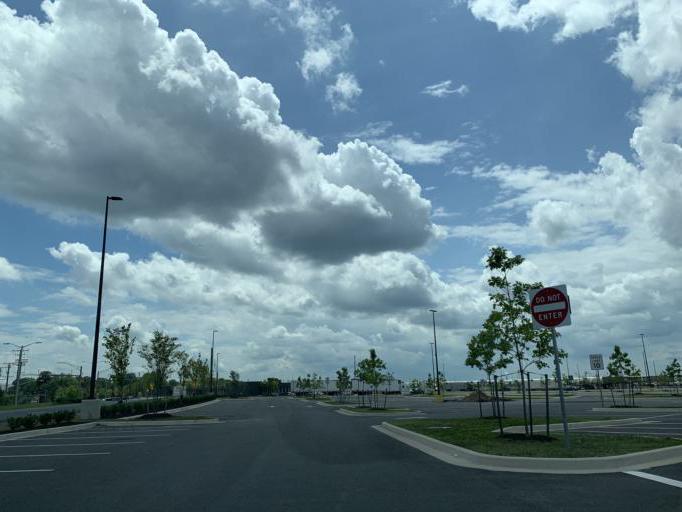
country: US
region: Maryland
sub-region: Baltimore County
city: Edgemere
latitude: 39.2272
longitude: -76.4688
